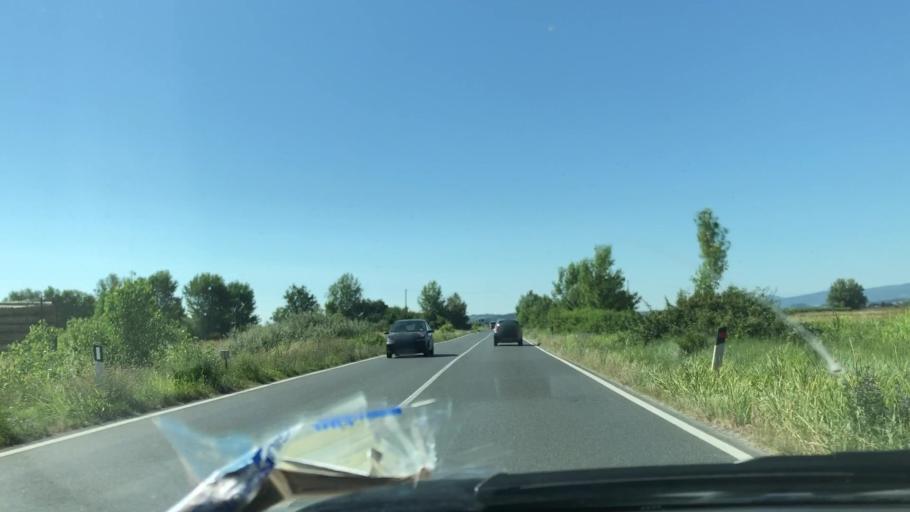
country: IT
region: Tuscany
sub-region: Province of Pisa
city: Forcoli
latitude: 43.5984
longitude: 10.6962
